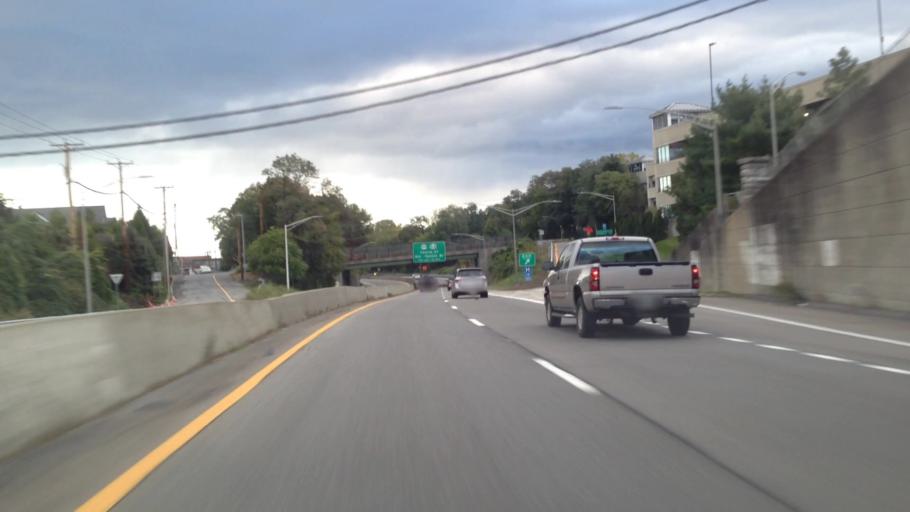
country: US
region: New York
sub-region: Dutchess County
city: Poughkeepsie
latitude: 41.6942
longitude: -73.9374
